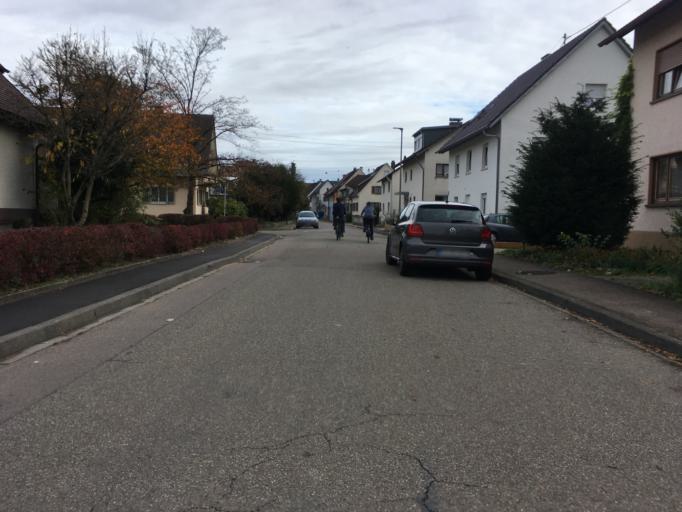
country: DE
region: Baden-Wuerttemberg
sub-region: Freiburg Region
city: Ihringen
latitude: 48.0407
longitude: 7.6447
